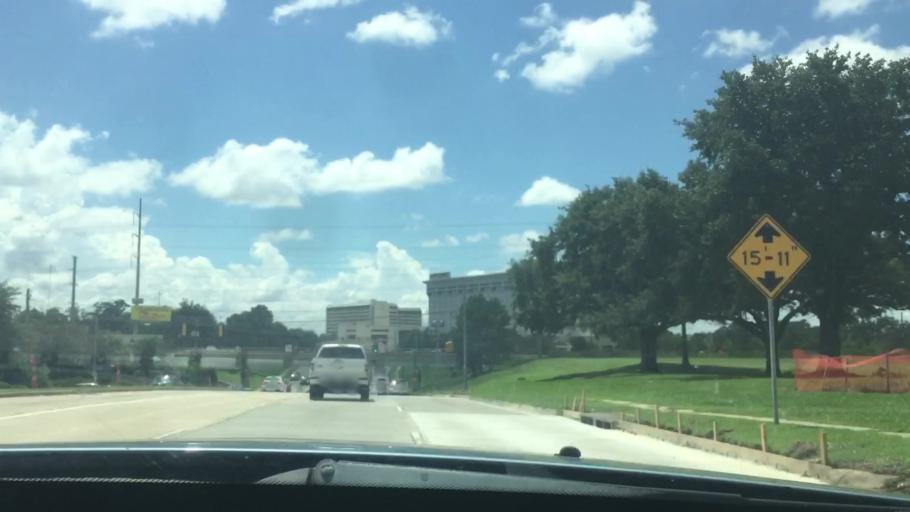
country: US
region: Louisiana
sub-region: East Baton Rouge Parish
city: Inniswold
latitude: 30.3920
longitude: -91.0909
